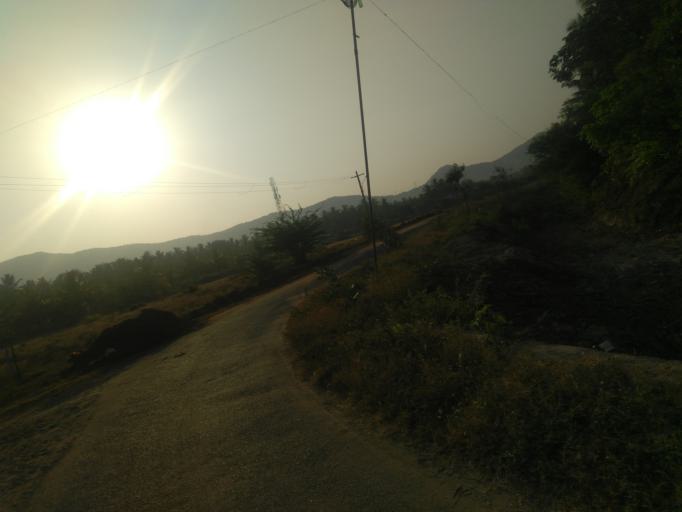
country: IN
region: Tamil Nadu
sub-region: Coimbatore
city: Karamadai
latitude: 11.2143
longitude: 76.8910
